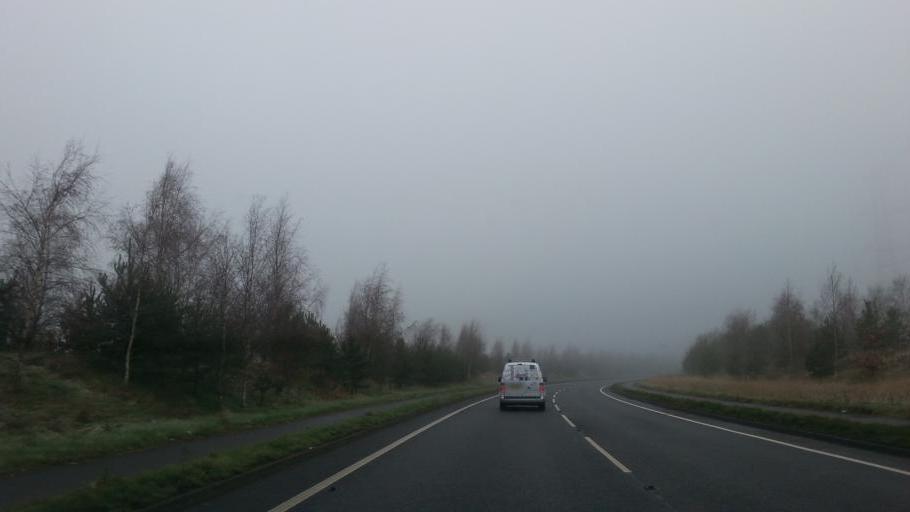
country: GB
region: England
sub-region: Cheshire East
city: Alderley Edge
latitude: 53.2895
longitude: -2.2542
